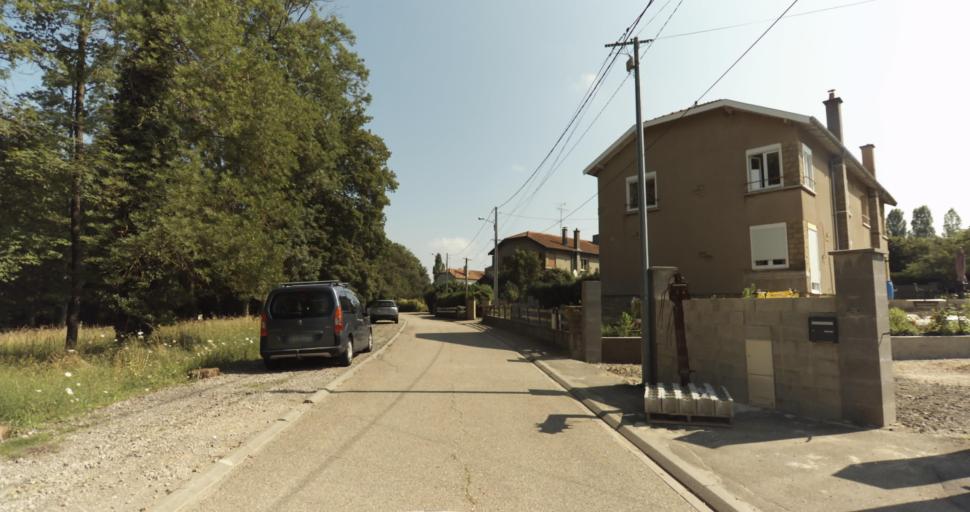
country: FR
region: Lorraine
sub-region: Departement de Meurthe-et-Moselle
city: Mancieulles
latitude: 49.2813
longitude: 5.8979
